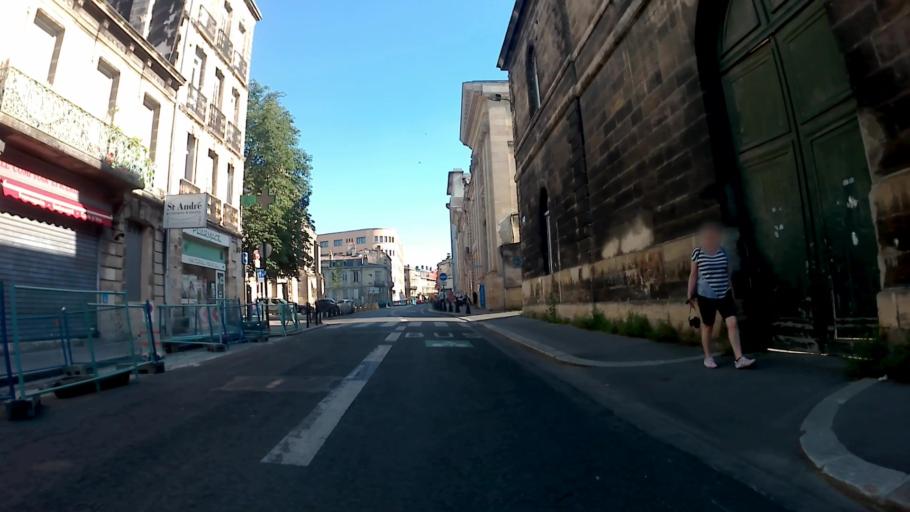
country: FR
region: Aquitaine
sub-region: Departement de la Gironde
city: Bordeaux
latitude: 44.8338
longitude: -0.5782
